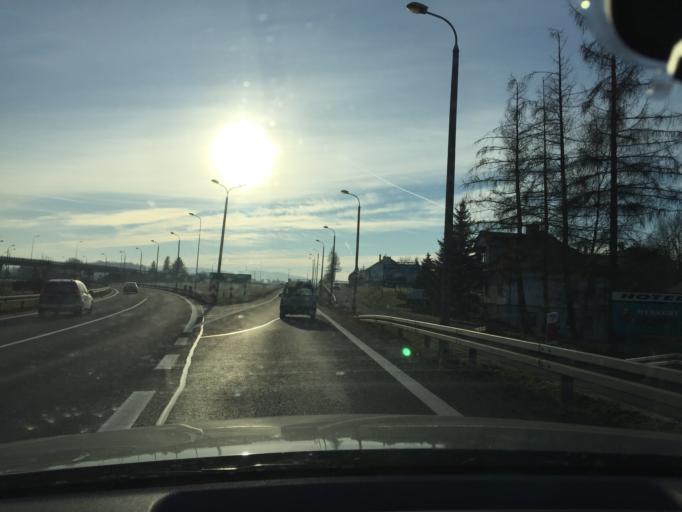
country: PL
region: Lesser Poland Voivodeship
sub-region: Powiat myslenicki
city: Glogoczow
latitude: 49.9104
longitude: 19.8699
